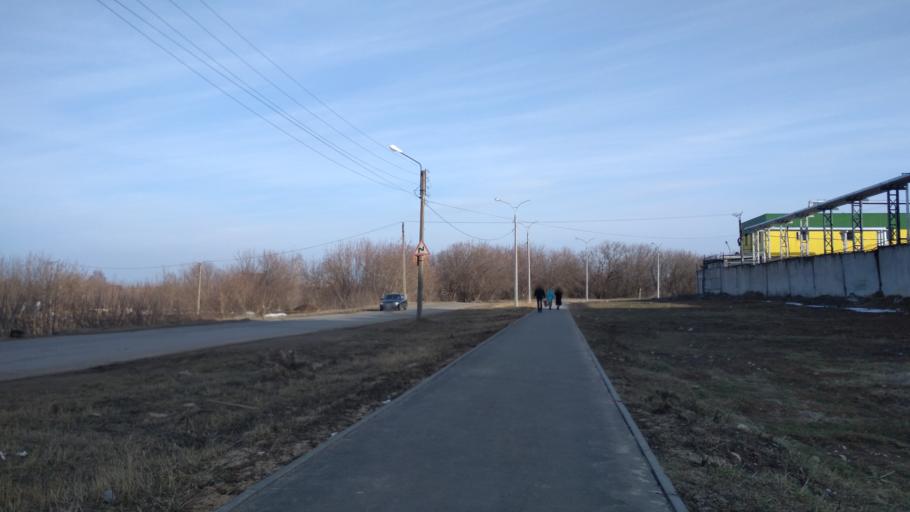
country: RU
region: Chuvashia
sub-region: Cheboksarskiy Rayon
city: Cheboksary
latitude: 56.1356
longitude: 47.3144
